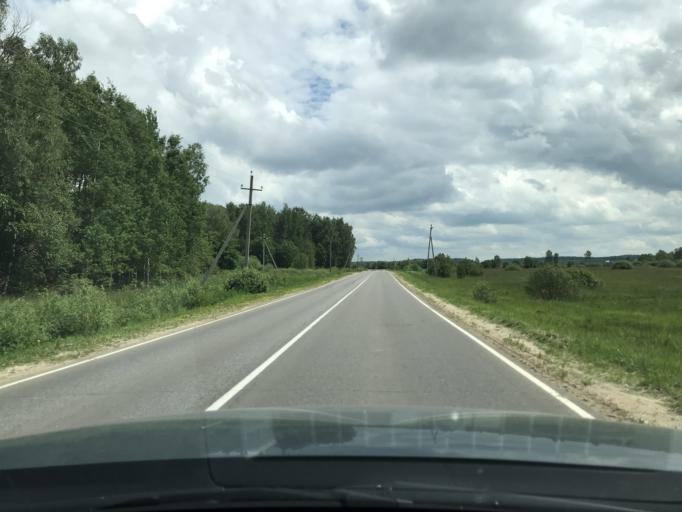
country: RU
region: Kaluga
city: Borovsk
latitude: 55.3654
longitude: 36.4080
